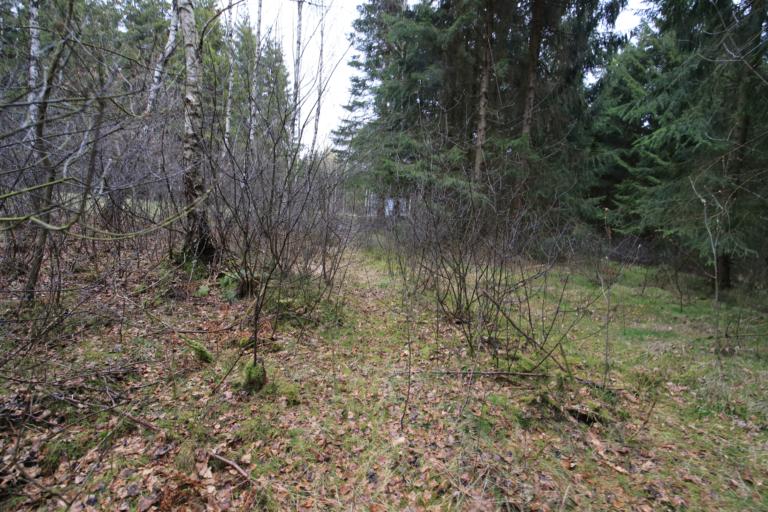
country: SE
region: Halland
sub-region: Varbergs Kommun
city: Tvaaker
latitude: 57.1510
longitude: 12.4577
